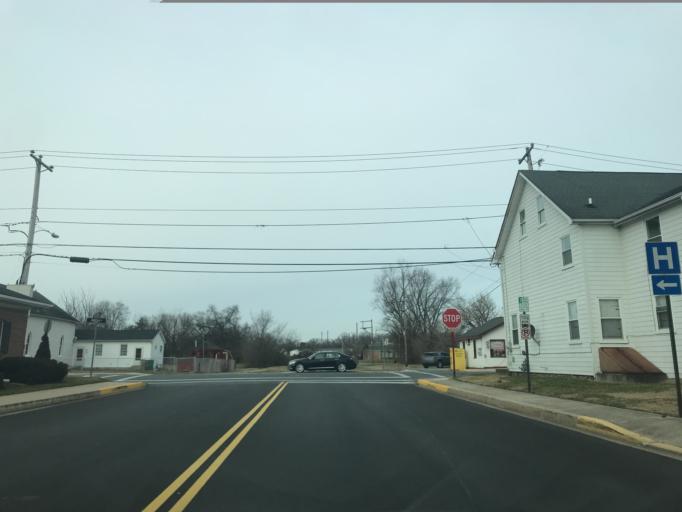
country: US
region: Maryland
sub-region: Cecil County
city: Elkton
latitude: 39.6100
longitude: -75.8269
